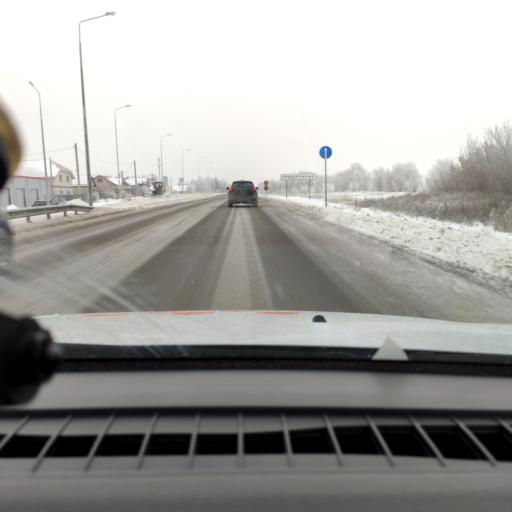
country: RU
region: Samara
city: Samara
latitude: 53.0880
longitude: 50.1556
